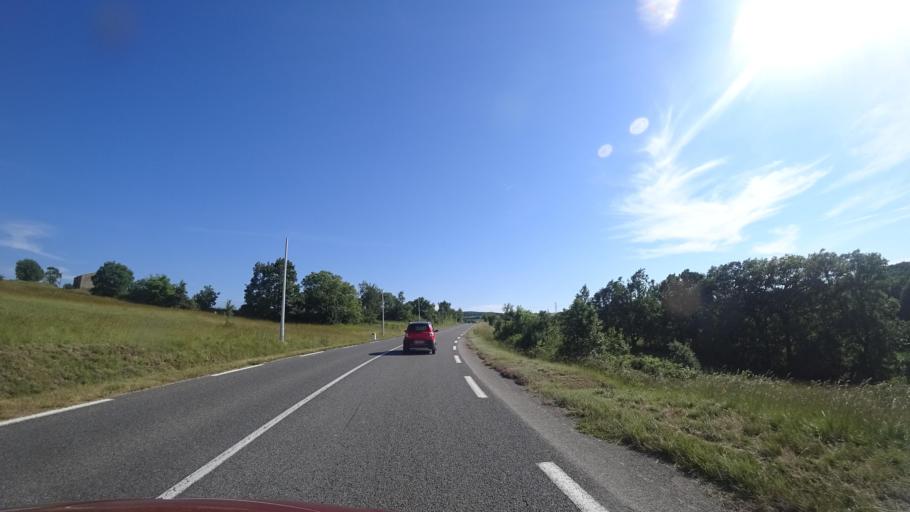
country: FR
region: Midi-Pyrenees
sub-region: Departement de l'Aveyron
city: Saint-Affrique
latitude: 44.0094
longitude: 2.9370
